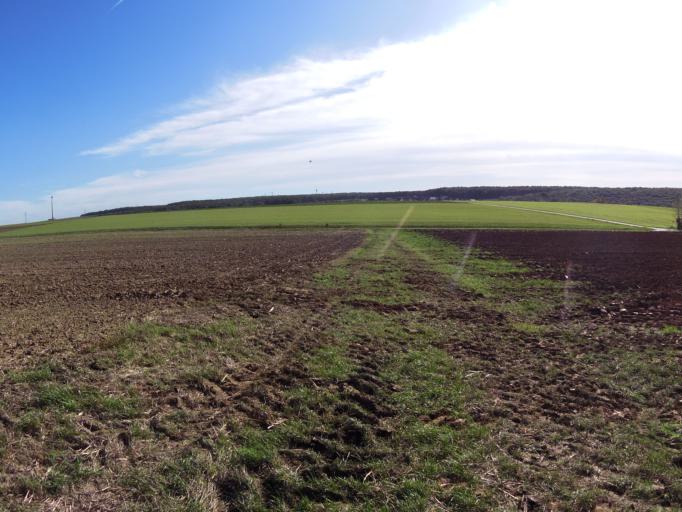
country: DE
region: Bavaria
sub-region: Regierungsbezirk Unterfranken
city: Theilheim
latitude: 49.7605
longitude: 10.0213
